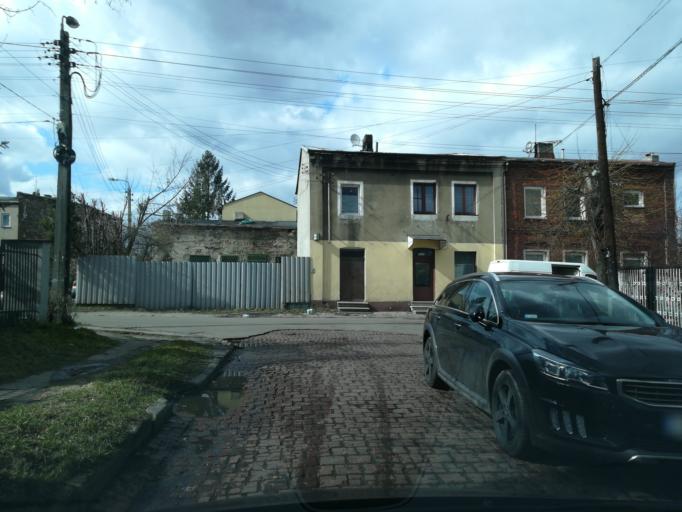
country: PL
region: Silesian Voivodeship
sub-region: Sosnowiec
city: Sosnowiec
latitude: 50.2911
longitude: 19.1286
